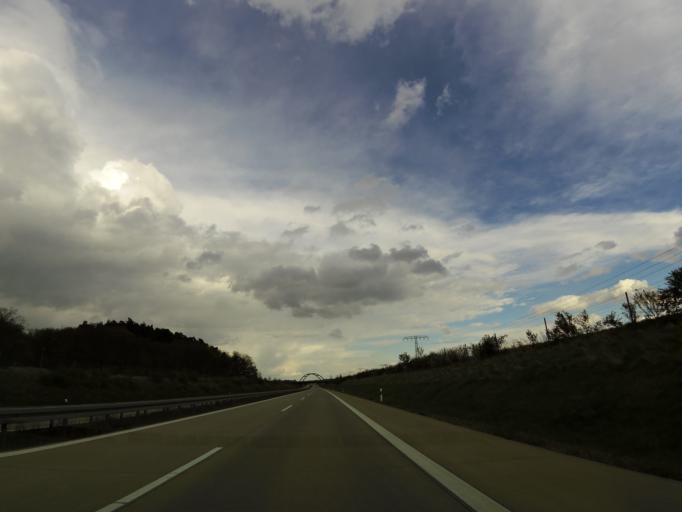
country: DE
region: Saxony-Anhalt
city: Blankenburg
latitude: 51.8053
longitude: 10.9712
